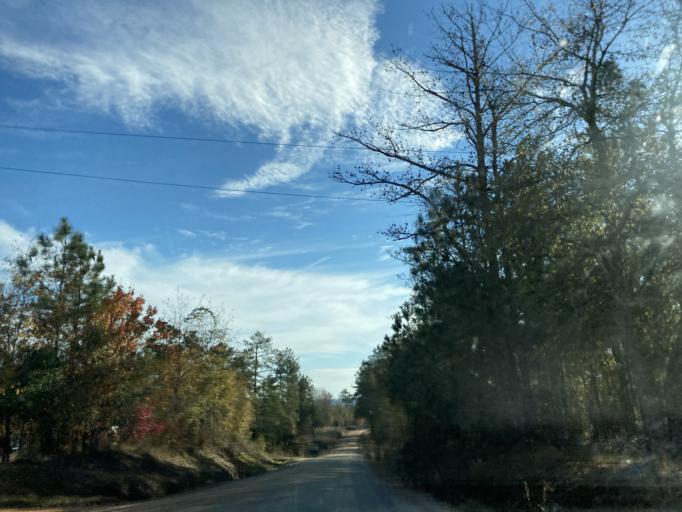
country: US
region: Georgia
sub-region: Jones County
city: Gray
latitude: 32.8905
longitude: -83.4882
